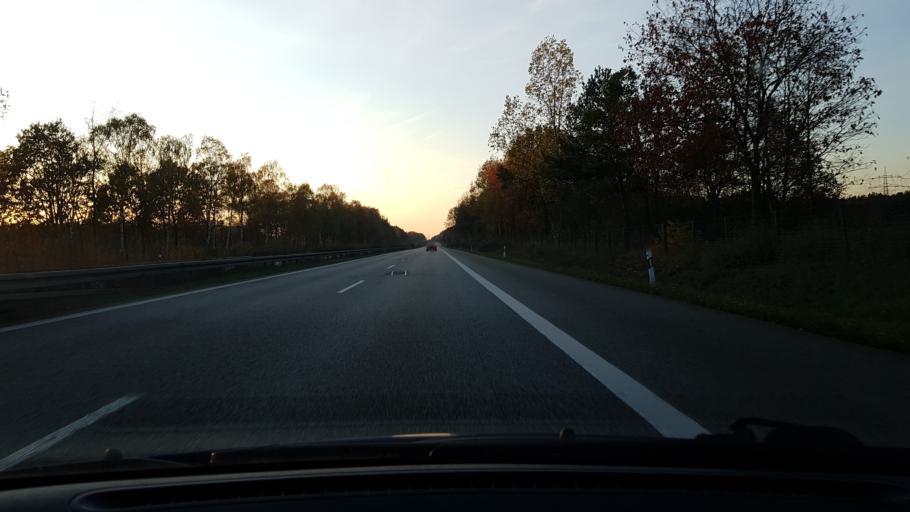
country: DE
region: Mecklenburg-Vorpommern
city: Wittenburg
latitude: 53.5068
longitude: 11.0049
